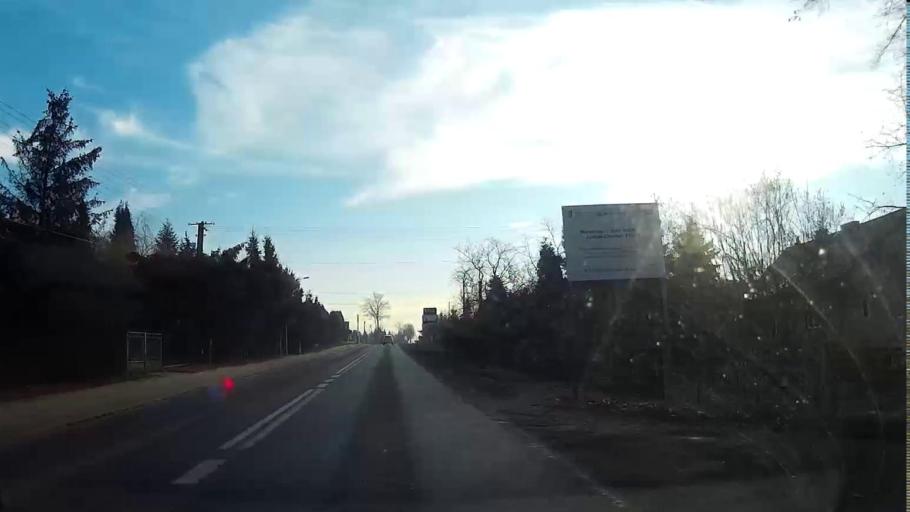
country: PL
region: Lesser Poland Voivodeship
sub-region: Powiat chrzanowski
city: Babice
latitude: 50.0740
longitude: 19.4387
